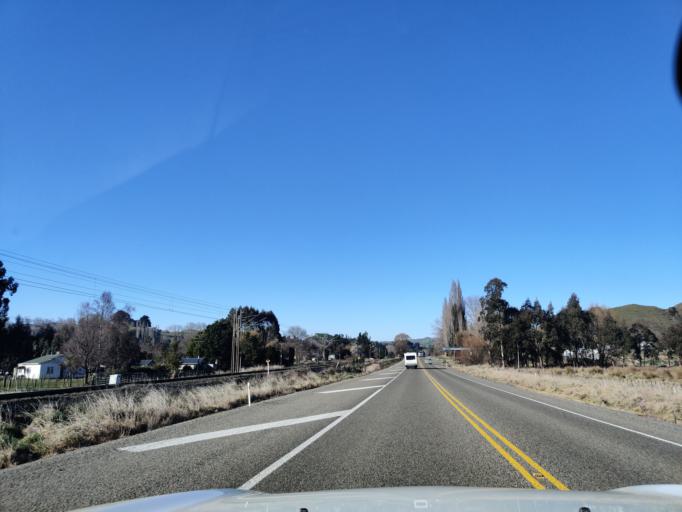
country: NZ
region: Manawatu-Wanganui
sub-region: Ruapehu District
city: Waiouru
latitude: -39.7279
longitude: 175.8429
